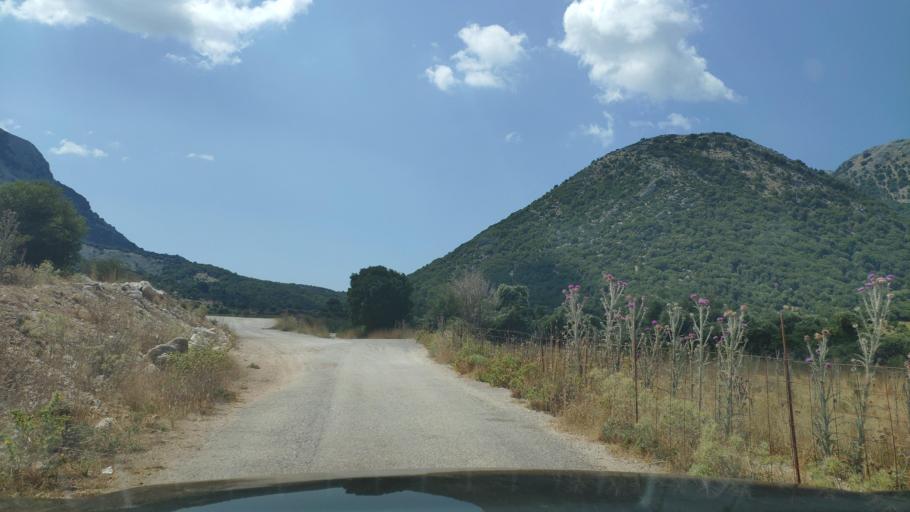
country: GR
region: West Greece
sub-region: Nomos Aitolias kai Akarnanias
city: Kandila
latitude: 38.7772
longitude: 20.9724
